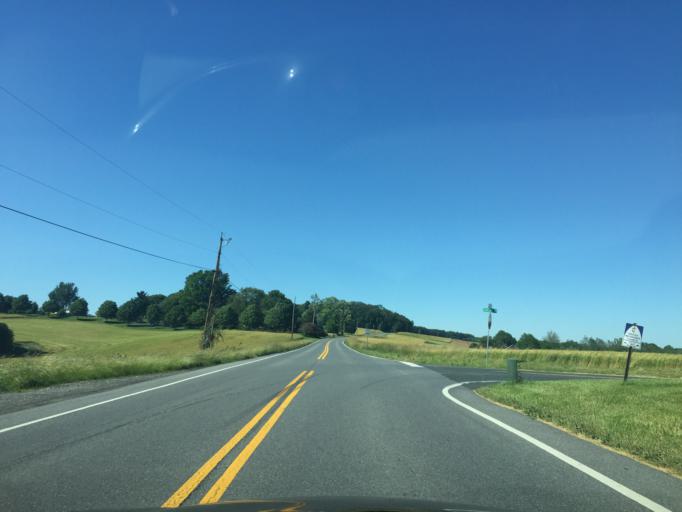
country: US
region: Maryland
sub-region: Carroll County
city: Hampstead
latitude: 39.6004
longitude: -76.9107
